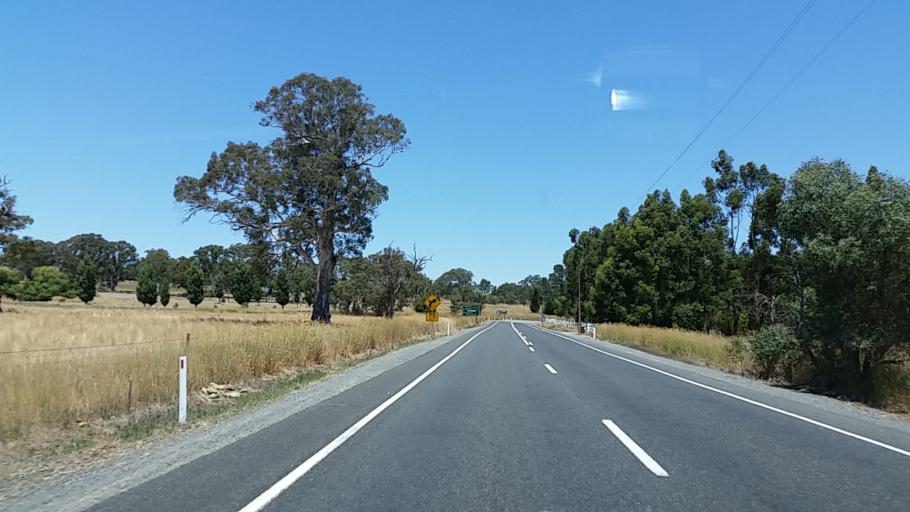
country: AU
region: South Australia
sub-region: Adelaide Hills
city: Birdwood
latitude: -34.7972
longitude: 139.0060
